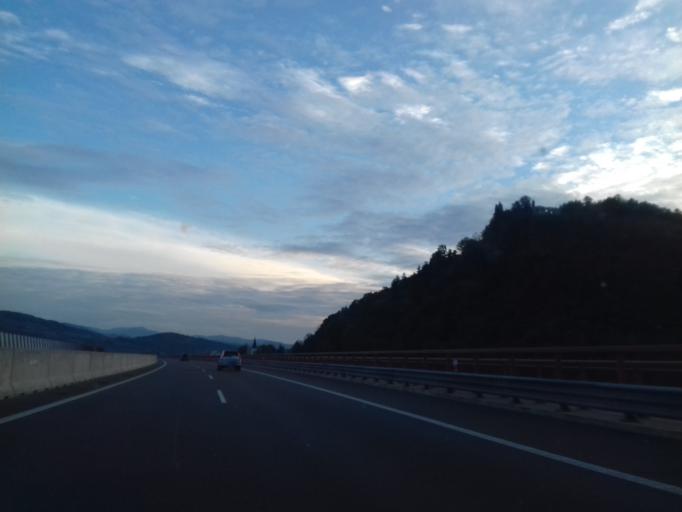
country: SK
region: Trenciansky
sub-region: Okres Povazska Bystrica
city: Povazska Bystrica
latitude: 49.1497
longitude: 18.4624
